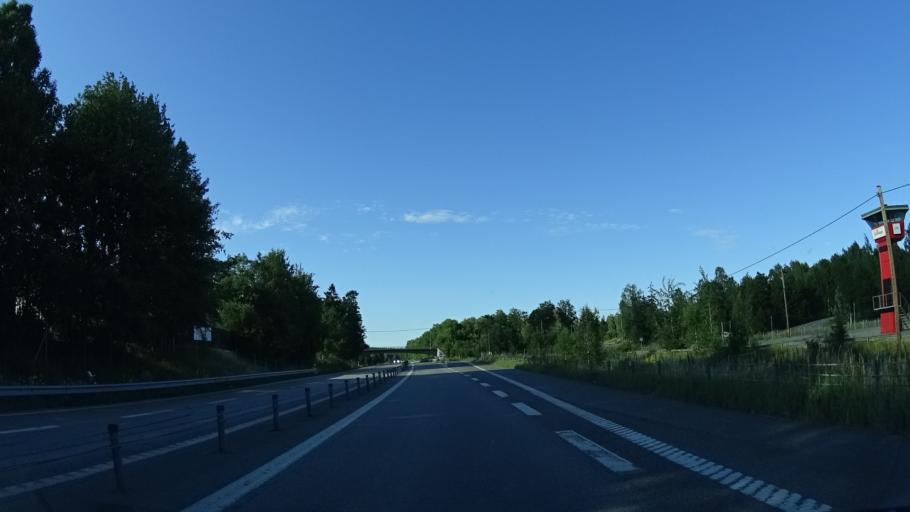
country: SE
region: Stockholm
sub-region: Vallentuna Kommun
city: Vallentuna
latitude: 59.5085
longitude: 18.1747
